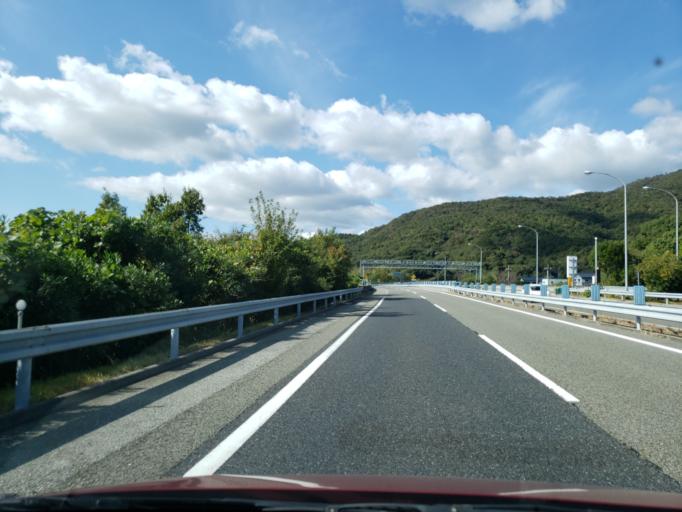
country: JP
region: Tokushima
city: Ishii
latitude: 34.1397
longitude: 134.4091
